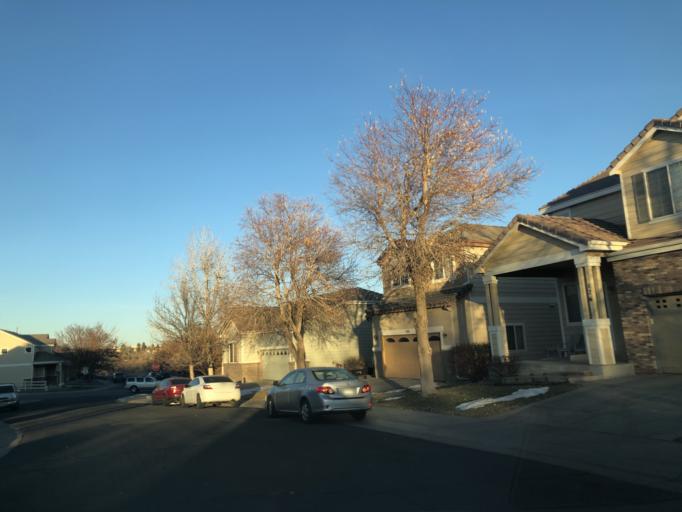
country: US
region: Colorado
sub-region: Adams County
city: Aurora
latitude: 39.7137
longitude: -104.8123
